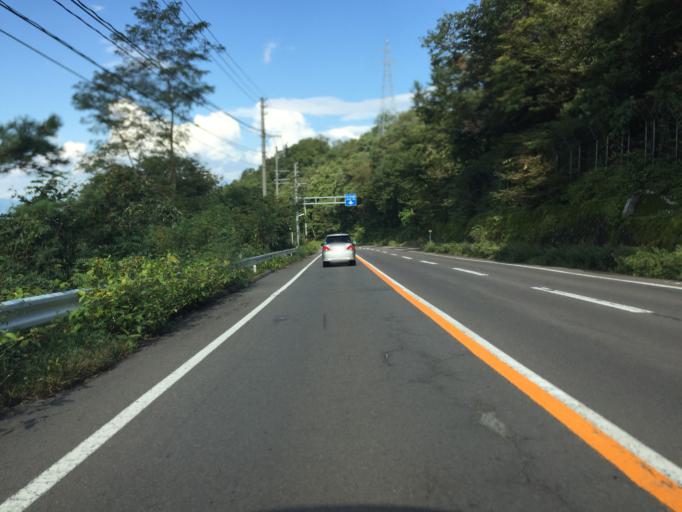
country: JP
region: Fukushima
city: Fukushima-shi
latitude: 37.6911
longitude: 140.3403
